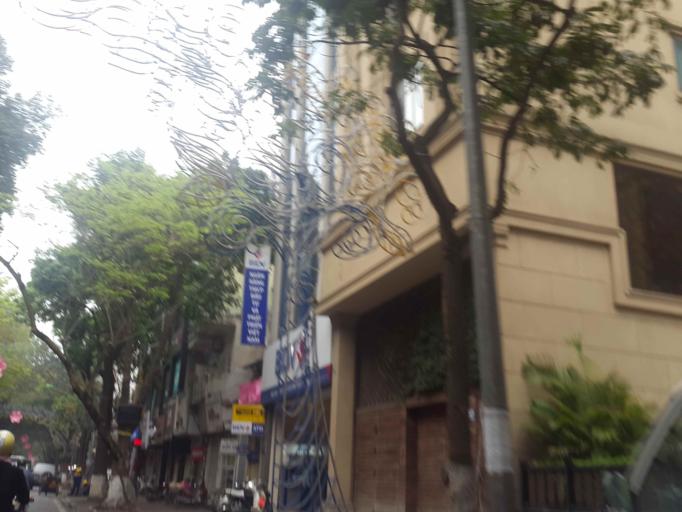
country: VN
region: Ha Noi
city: Hoan Kiem
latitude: 21.0404
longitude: 105.8427
